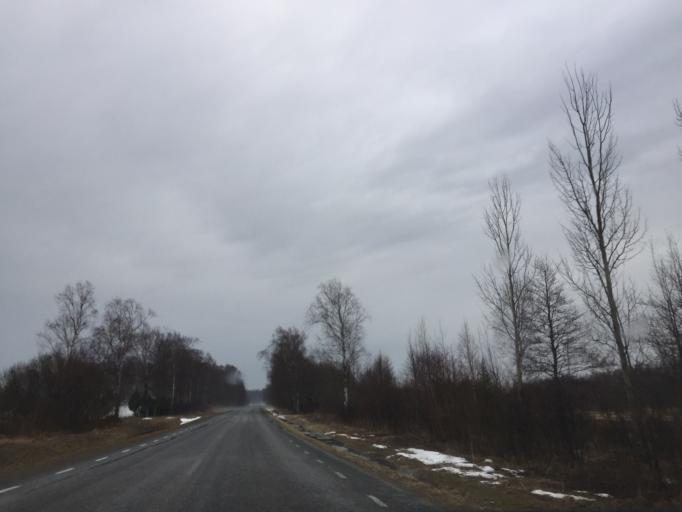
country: EE
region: Saare
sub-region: Orissaare vald
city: Orissaare
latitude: 58.5719
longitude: 23.0323
